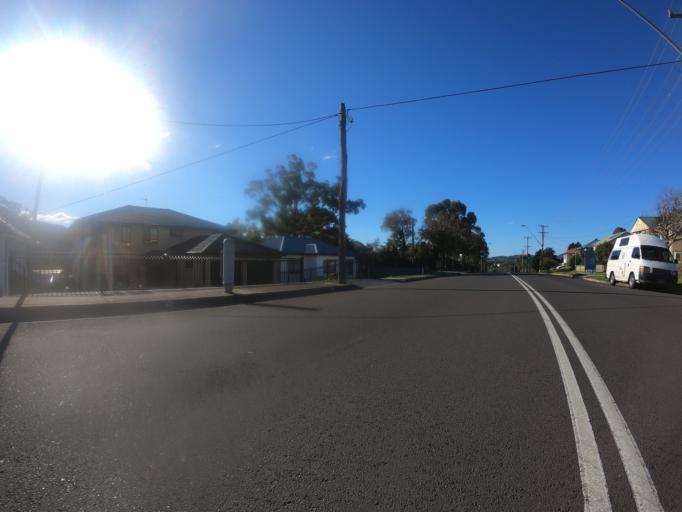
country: AU
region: New South Wales
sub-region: Wollongong
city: Cordeaux Heights
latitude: -34.4614
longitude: 150.8350
